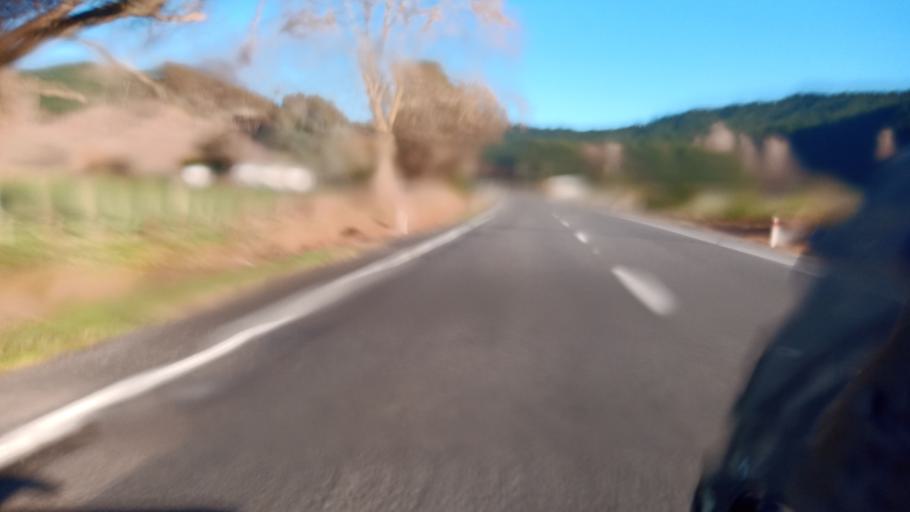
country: NZ
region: Hawke's Bay
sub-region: Wairoa District
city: Wairoa
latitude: -39.0206
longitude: 177.3238
